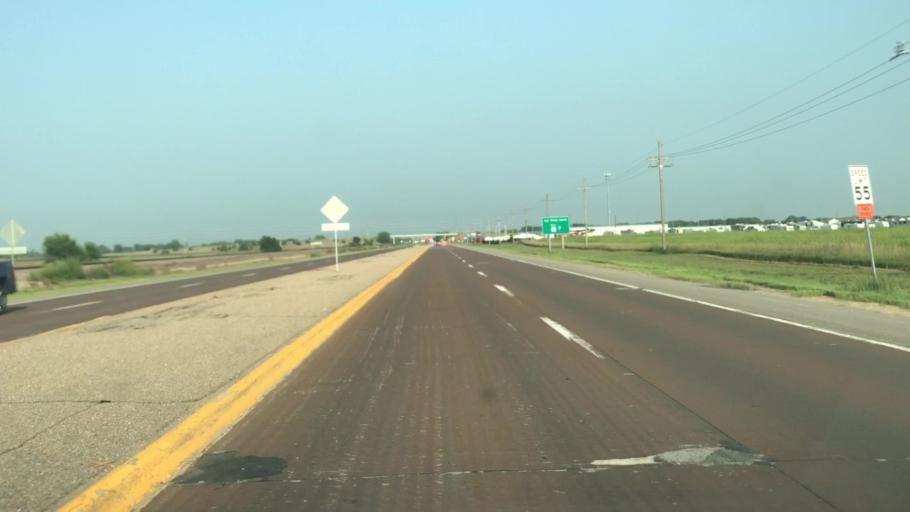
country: US
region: Nebraska
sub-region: Hall County
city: Grand Island
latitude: 40.9563
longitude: -98.3969
